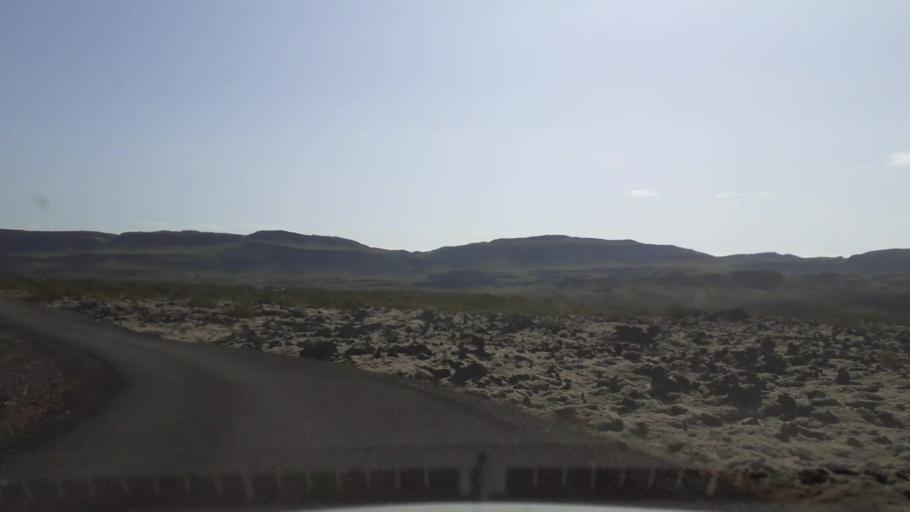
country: IS
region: West
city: Borgarnes
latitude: 64.7577
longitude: -21.5578
